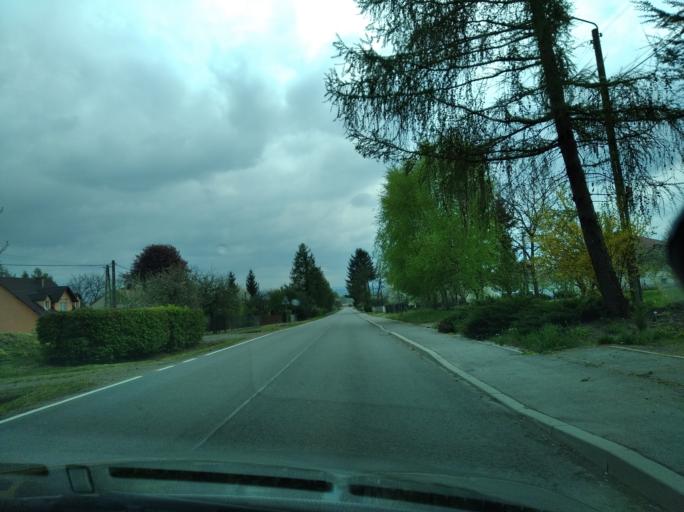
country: PL
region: Subcarpathian Voivodeship
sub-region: Powiat brzozowski
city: Jasionow
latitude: 49.6503
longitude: 21.9770
